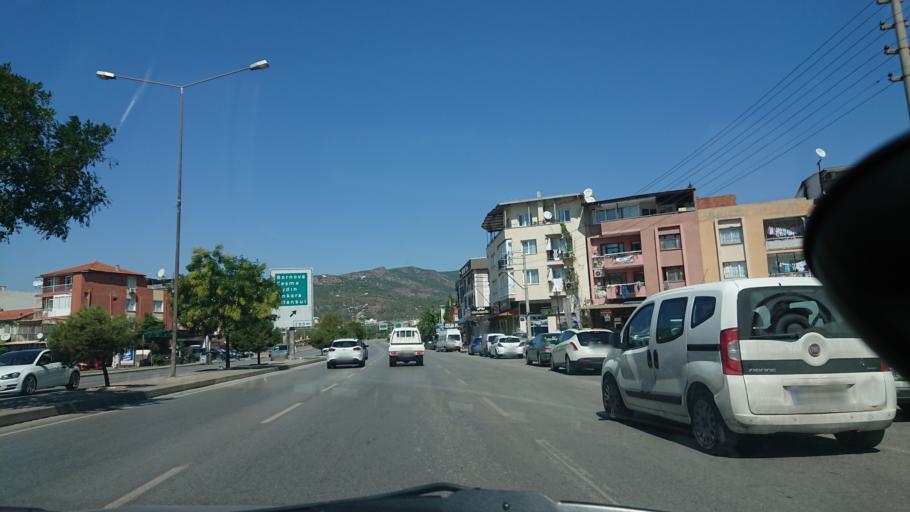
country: TR
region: Izmir
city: Karsiyaka
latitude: 38.4804
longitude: 27.1151
